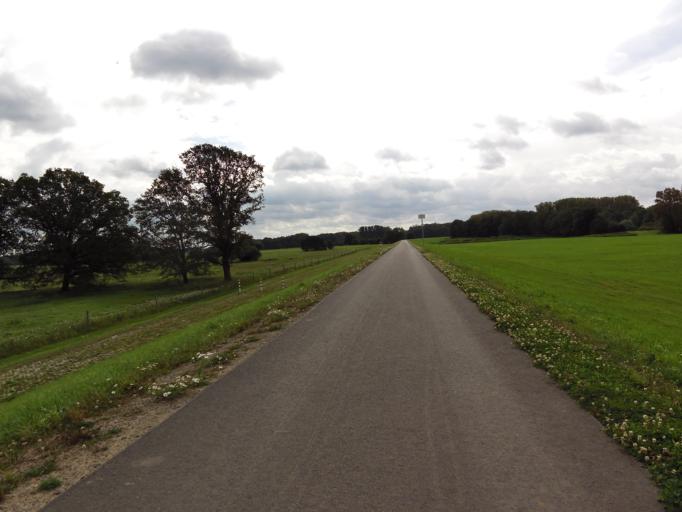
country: DE
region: Saxony-Anhalt
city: Havelberg
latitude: 52.8436
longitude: 12.0455
